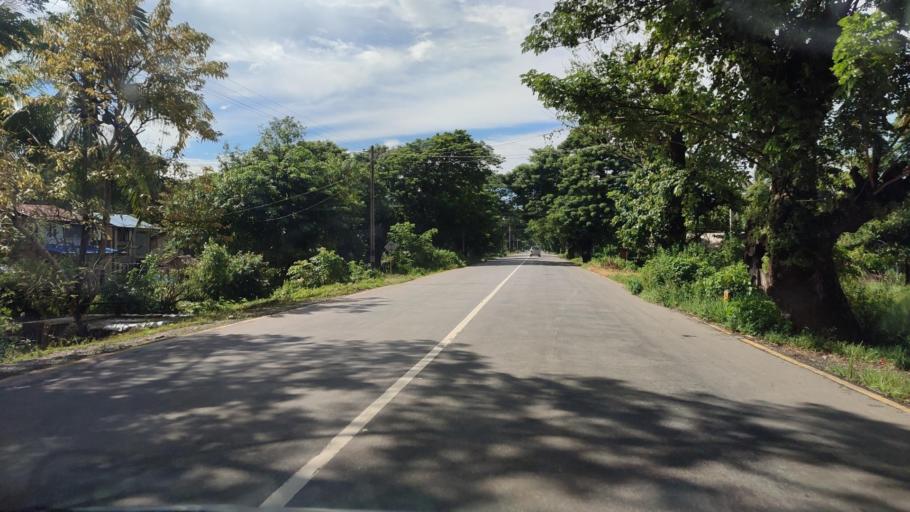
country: MM
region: Bago
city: Pyu
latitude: 18.2534
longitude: 96.5325
